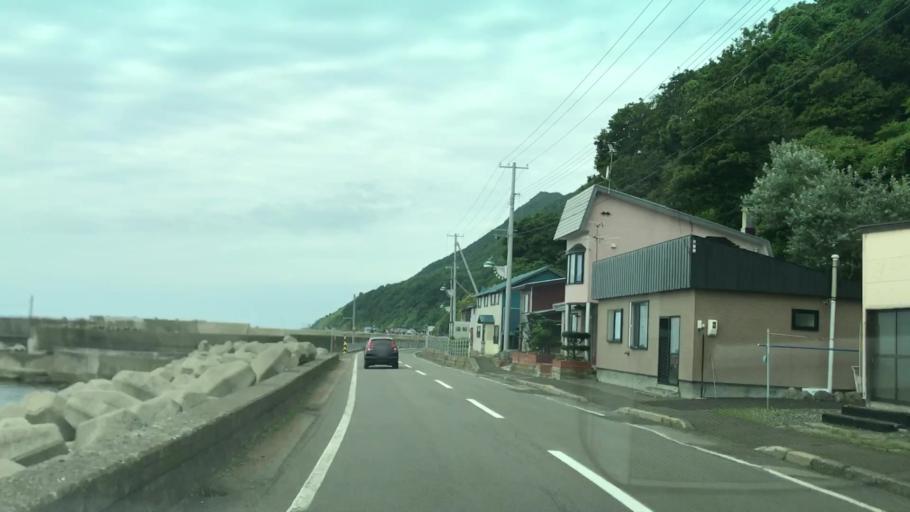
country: JP
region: Hokkaido
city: Iwanai
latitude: 43.1557
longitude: 140.4059
